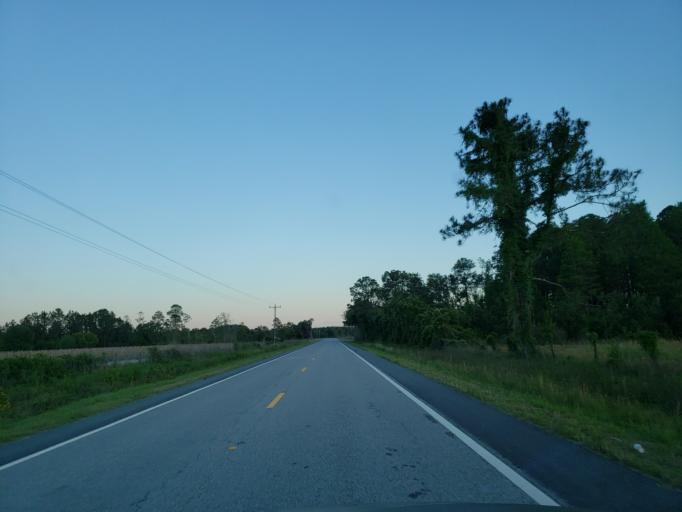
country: US
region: Georgia
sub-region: Echols County
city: Statenville
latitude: 30.5677
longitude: -83.1576
